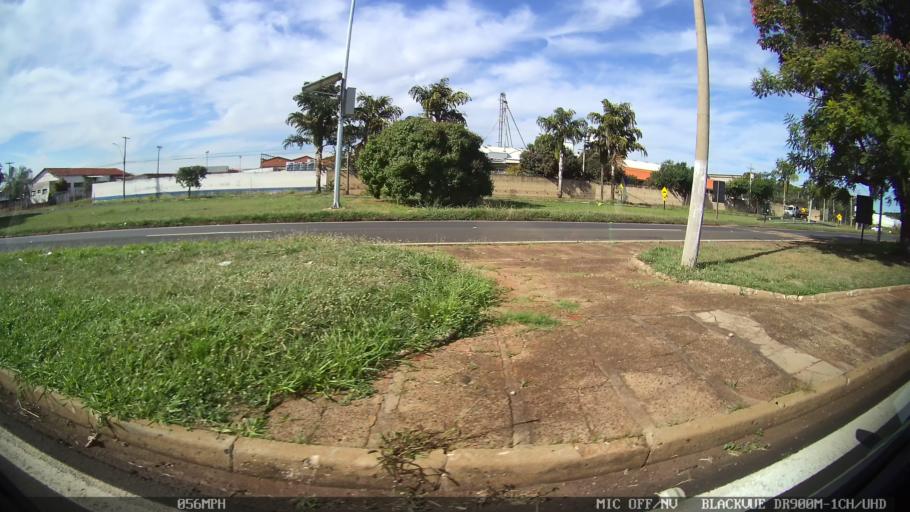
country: BR
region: Sao Paulo
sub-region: Araraquara
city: Araraquara
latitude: -21.8305
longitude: -48.1537
